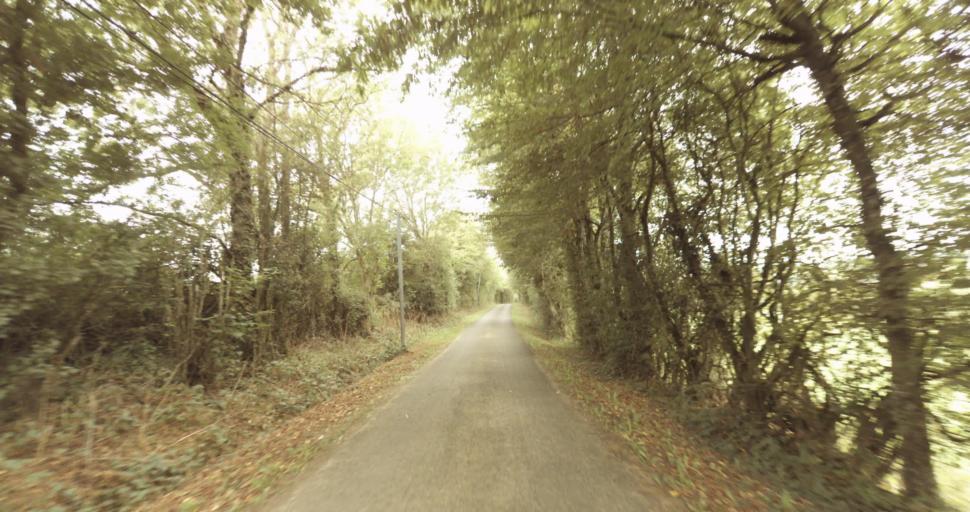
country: FR
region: Lower Normandy
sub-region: Departement de l'Orne
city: Gace
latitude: 48.7280
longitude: 0.3166
